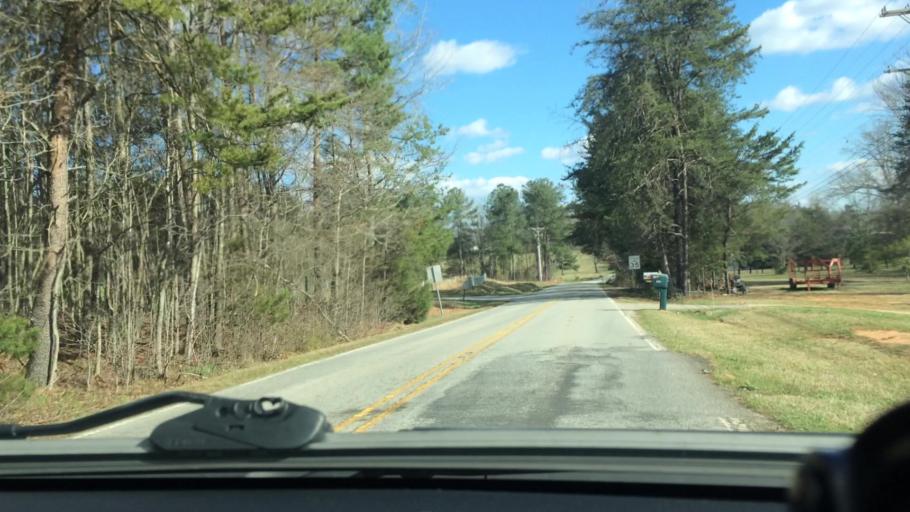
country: US
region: South Carolina
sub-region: Anderson County
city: Powdersville
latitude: 34.7964
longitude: -82.5421
